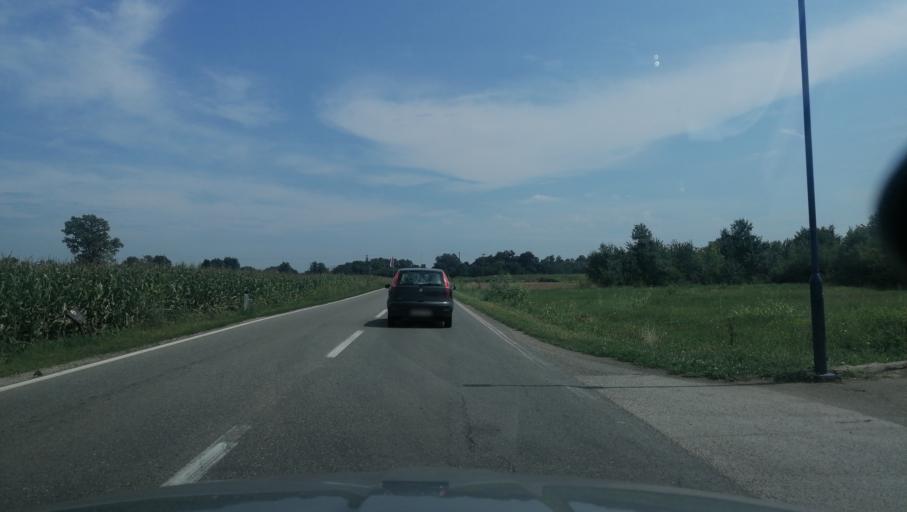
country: BA
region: Republika Srpska
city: Velika Obarska
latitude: 44.8262
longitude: 19.0355
